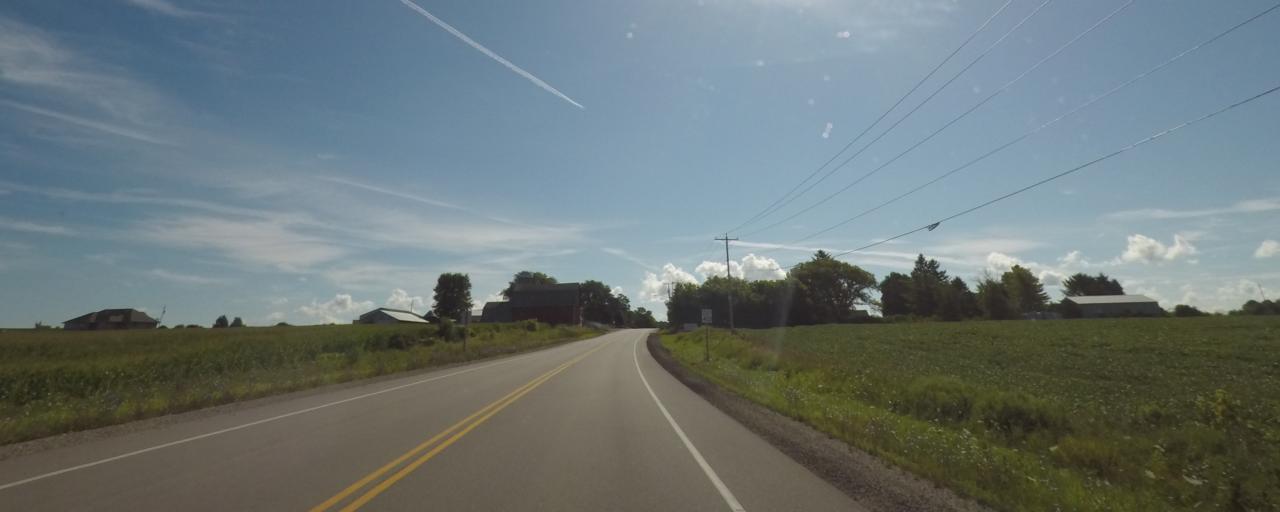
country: US
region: Wisconsin
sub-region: Jefferson County
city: Johnson Creek
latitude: 43.0758
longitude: -88.6751
